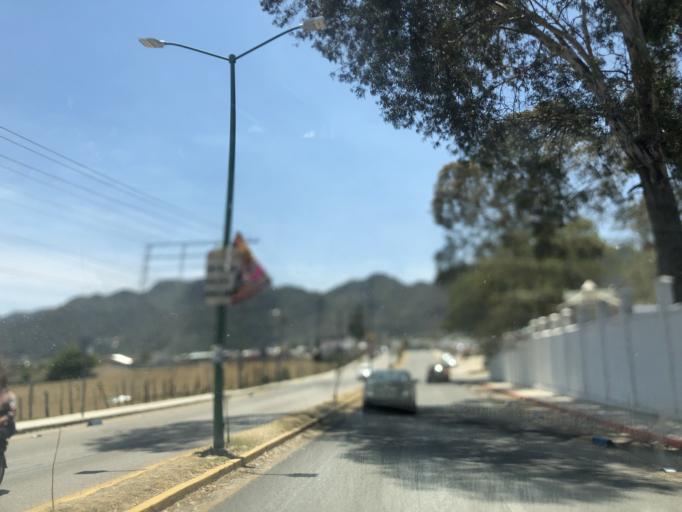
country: MX
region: Chiapas
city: San Cristobal de las Casas
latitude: 16.7248
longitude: -92.6516
